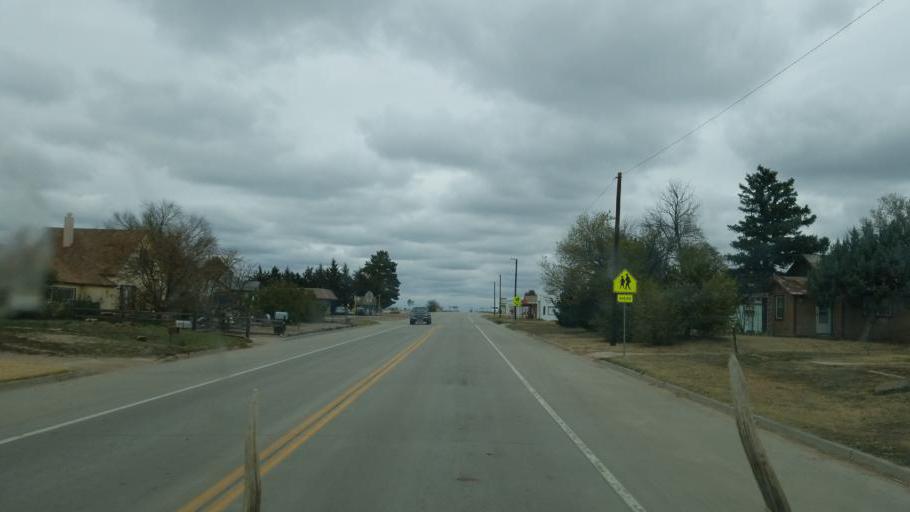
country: US
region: Colorado
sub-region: Kiowa County
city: Eads
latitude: 38.4821
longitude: -102.7858
